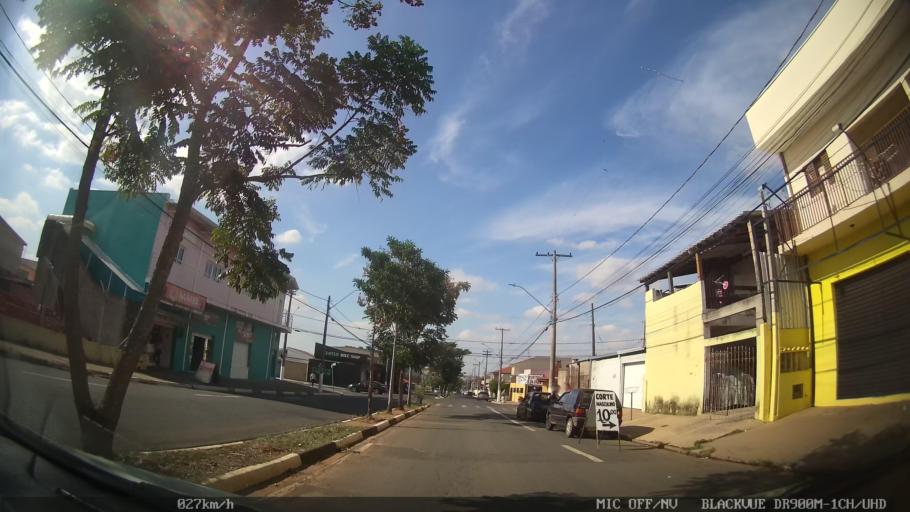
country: BR
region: Sao Paulo
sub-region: Hortolandia
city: Hortolandia
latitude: -22.9001
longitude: -47.2500
